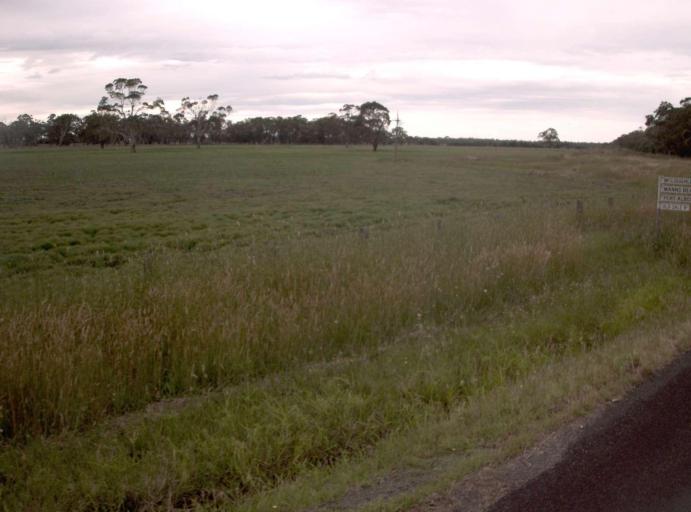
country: AU
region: Victoria
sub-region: Latrobe
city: Traralgon
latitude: -38.5597
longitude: 146.8051
